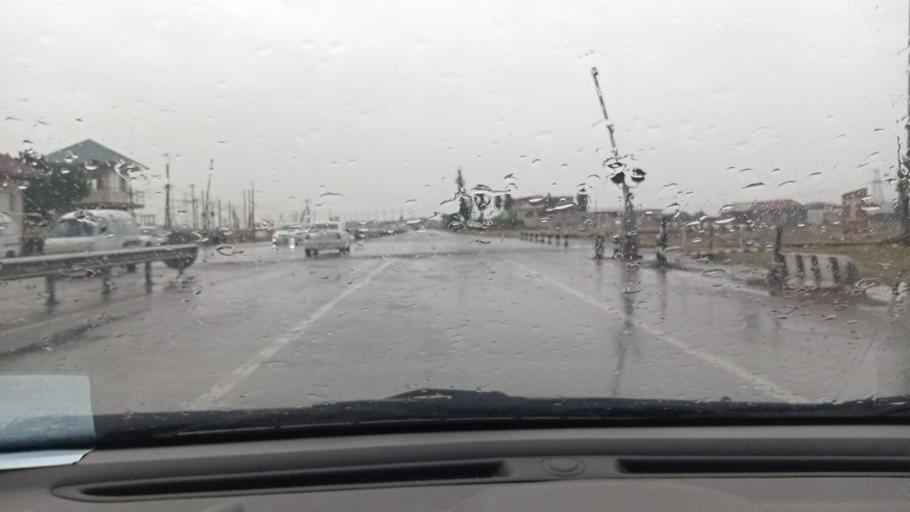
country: UZ
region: Toshkent
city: Ohangaron
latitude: 40.8998
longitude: 69.6576
